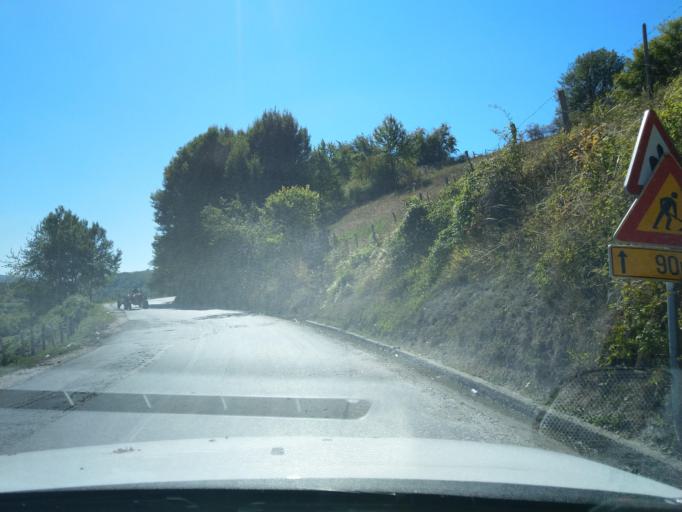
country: RS
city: Sokolovica
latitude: 43.2597
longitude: 20.2322
